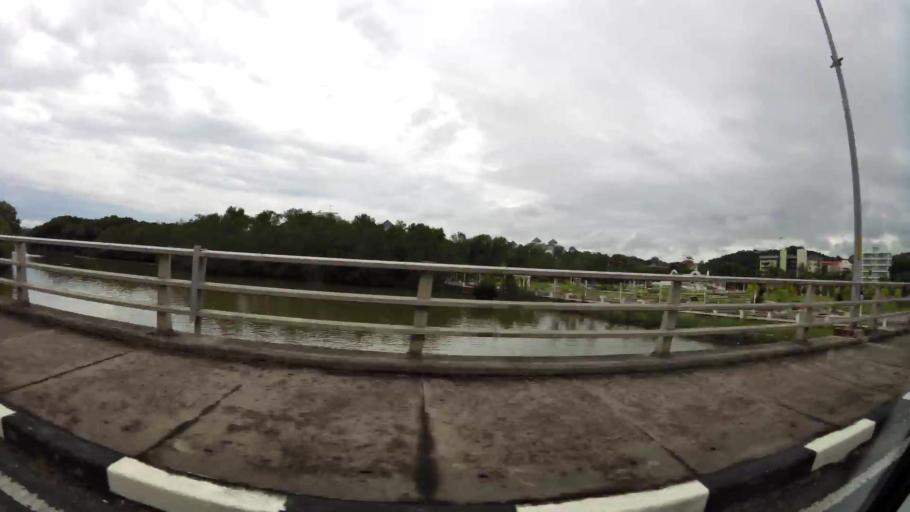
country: BN
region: Brunei and Muara
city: Bandar Seri Begawan
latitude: 4.8978
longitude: 114.9337
